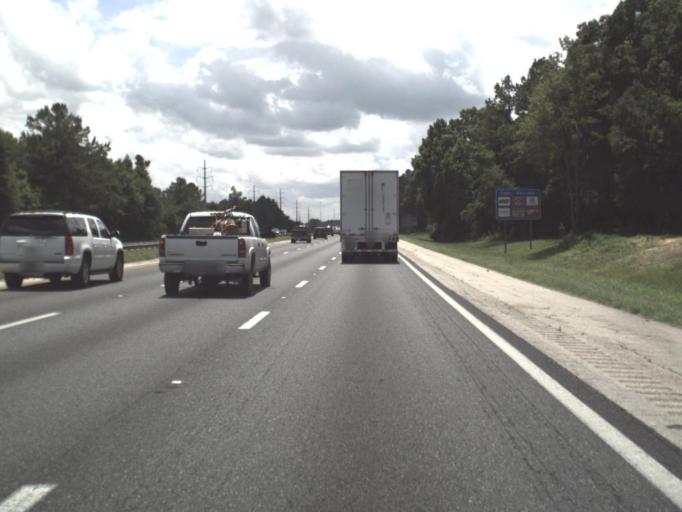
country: US
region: Florida
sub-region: Alachua County
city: Gainesville
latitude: 29.6303
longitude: -82.3954
